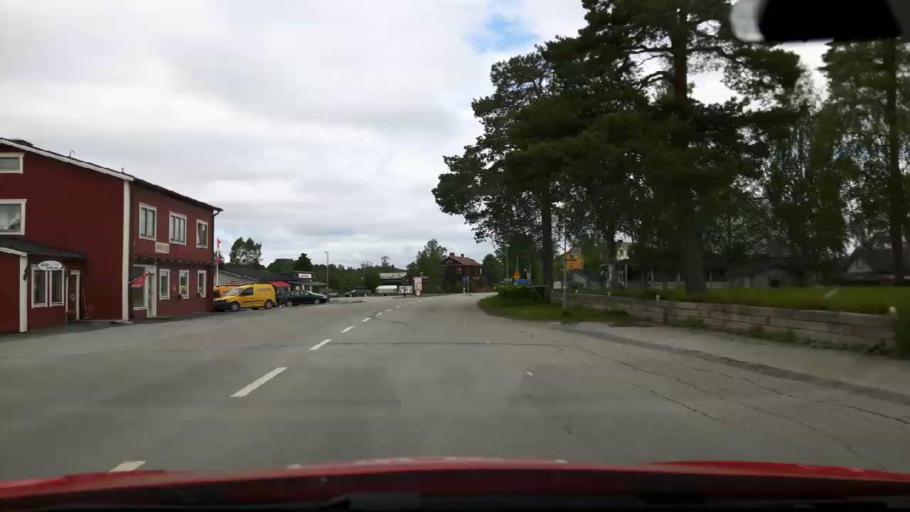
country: SE
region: Jaemtland
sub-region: Krokoms Kommun
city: Krokom
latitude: 63.3021
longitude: 14.4731
